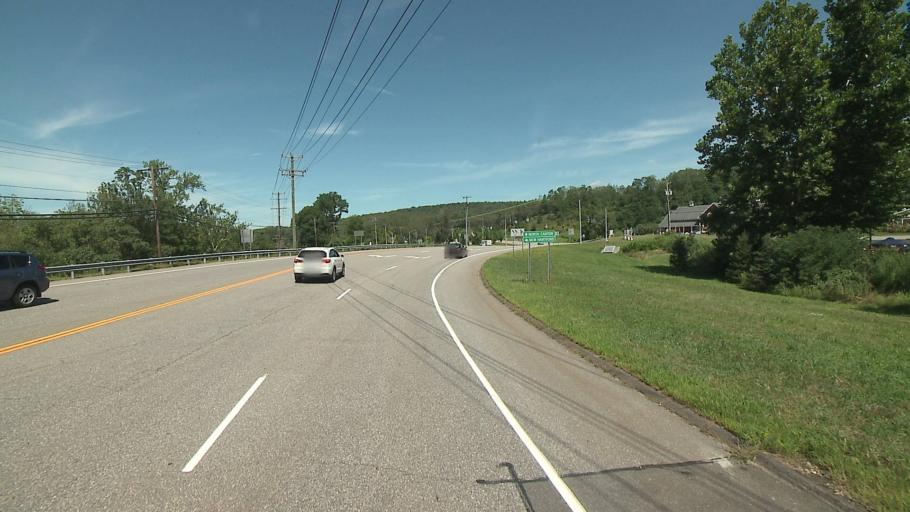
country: US
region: Connecticut
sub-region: Hartford County
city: Collinsville
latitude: 41.8339
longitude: -72.9280
